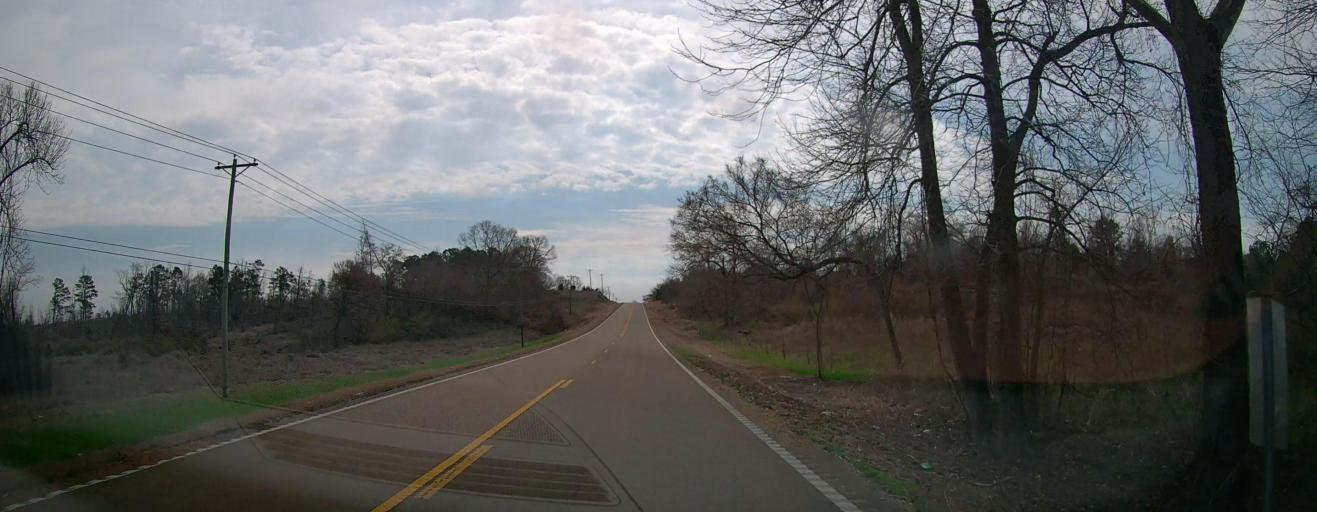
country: US
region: Mississippi
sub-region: Marshall County
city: Holly Springs
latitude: 34.7422
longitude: -89.4255
